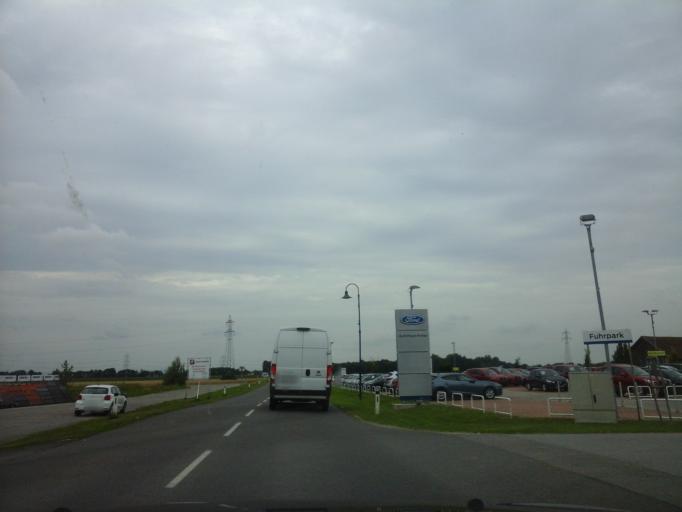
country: AT
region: Lower Austria
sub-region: Politischer Bezirk Ganserndorf
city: Mannsdorf an der Donau
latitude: 48.1534
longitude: 16.6582
